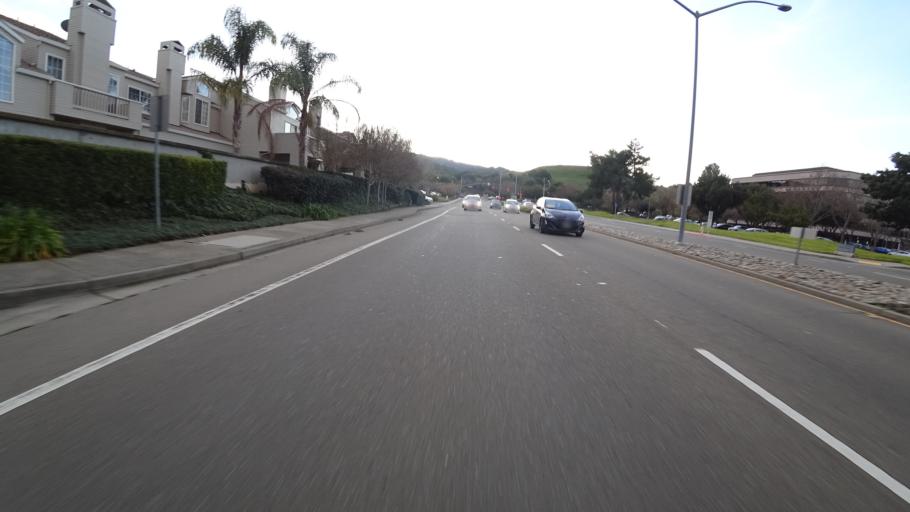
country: US
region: California
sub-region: Alameda County
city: Dublin
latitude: 37.6892
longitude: -121.9286
